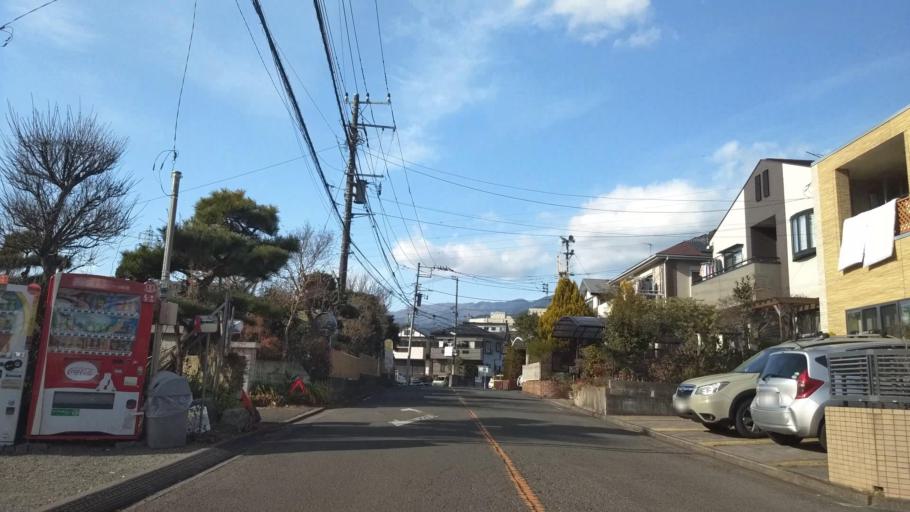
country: JP
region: Kanagawa
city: Hadano
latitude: 35.3807
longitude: 139.2431
